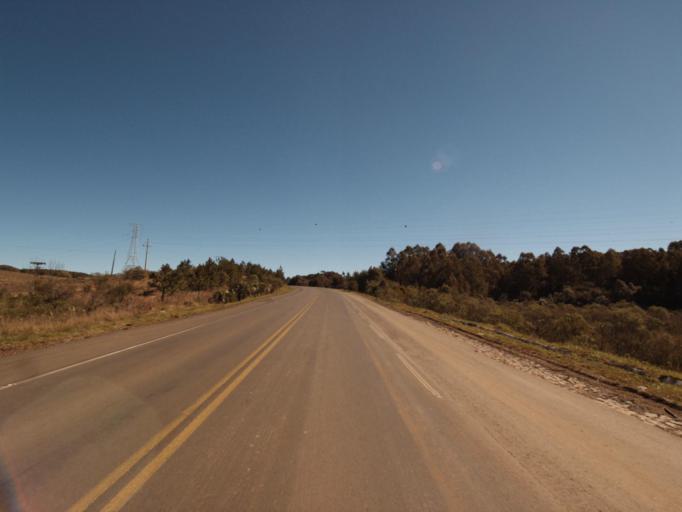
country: BR
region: Santa Catarina
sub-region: Concordia
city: Concordia
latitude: -26.9175
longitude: -51.8910
